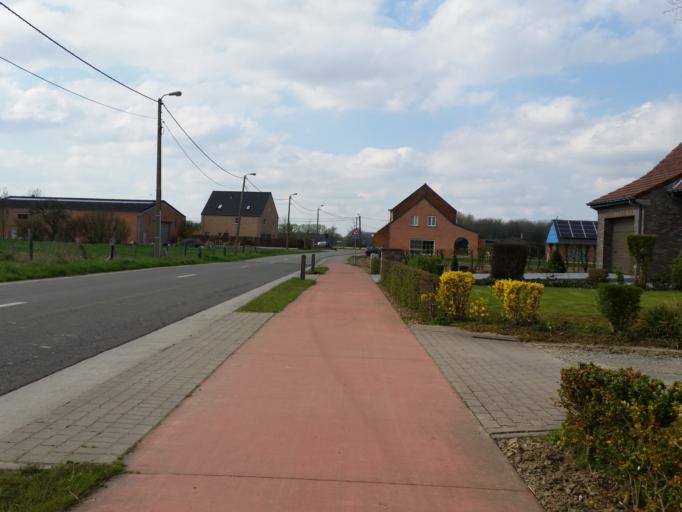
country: BE
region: Flanders
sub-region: Provincie Vlaams-Brabant
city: Kampenhout
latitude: 50.9410
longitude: 4.5348
